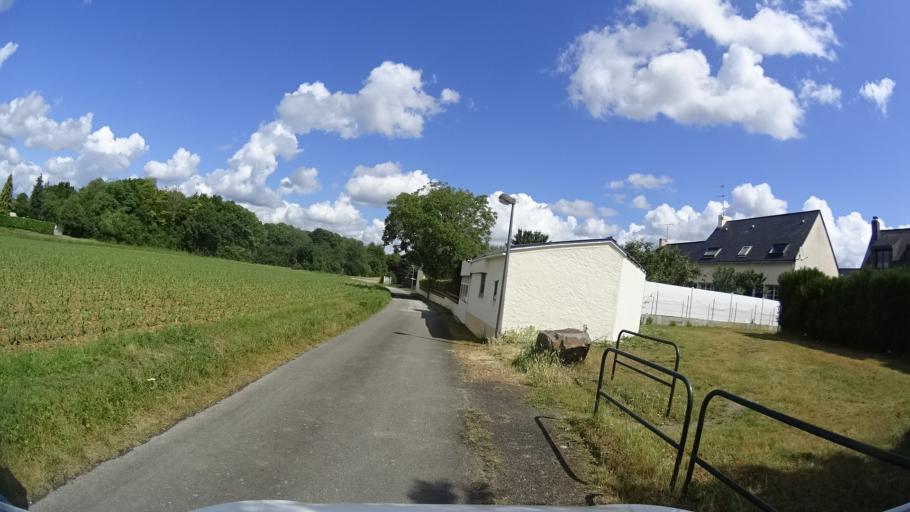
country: FR
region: Brittany
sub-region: Departement d'Ille-et-Vilaine
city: Chartres-de-Bretagne
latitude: 48.0382
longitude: -1.7138
